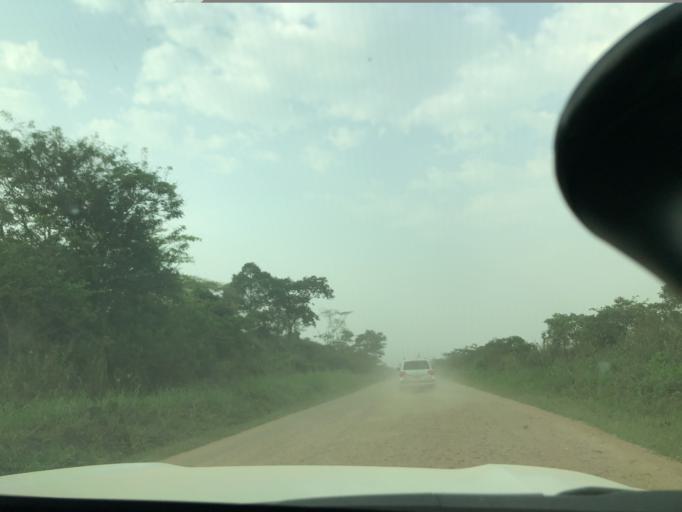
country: UG
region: Western Region
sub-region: Kasese District
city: Margherita
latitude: 0.2468
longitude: 29.6789
